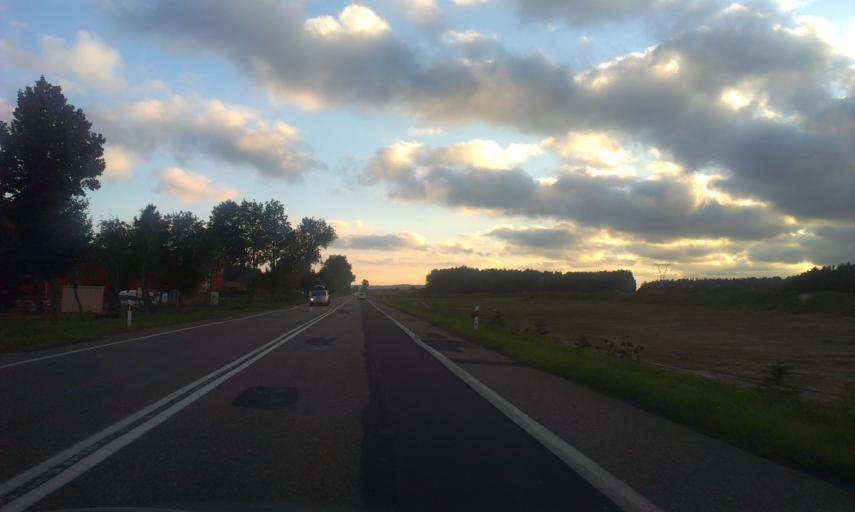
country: PL
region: West Pomeranian Voivodeship
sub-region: Powiat koszalinski
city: Sianow
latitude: 54.2475
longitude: 16.3479
